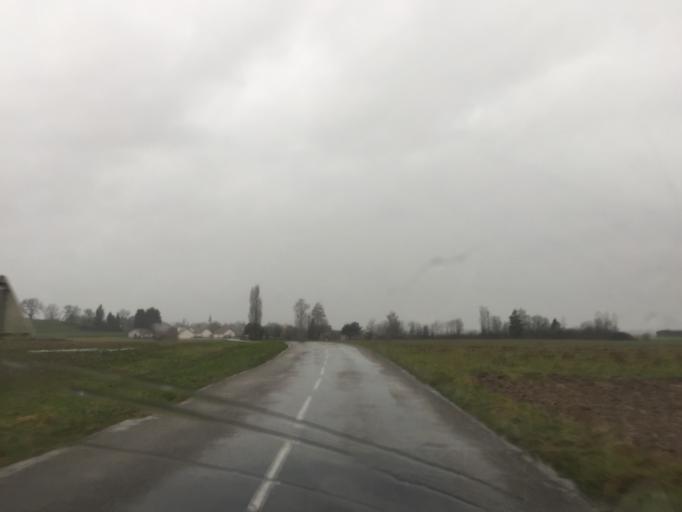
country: FR
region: Franche-Comte
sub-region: Departement du Doubs
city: Arc-et-Senans
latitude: 47.0014
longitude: 5.7698
